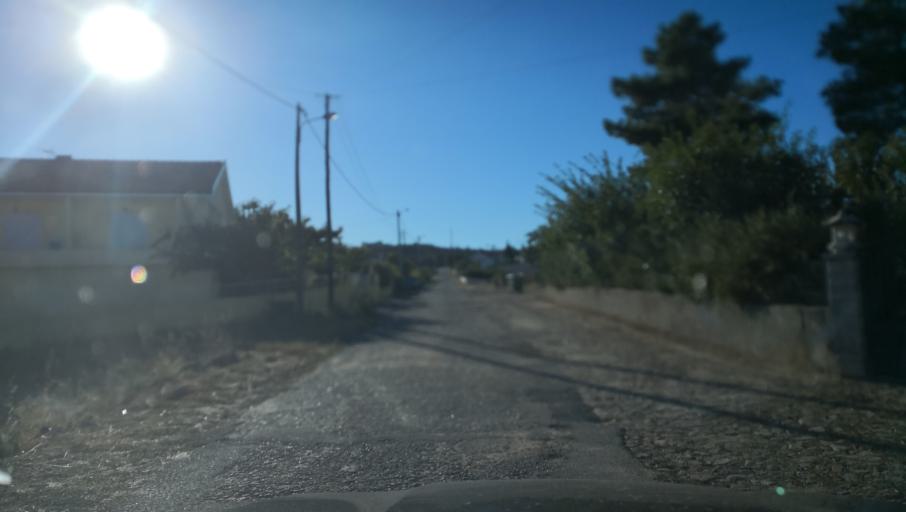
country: PT
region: Vila Real
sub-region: Sabrosa
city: Sabrosa
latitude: 41.3263
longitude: -7.5990
